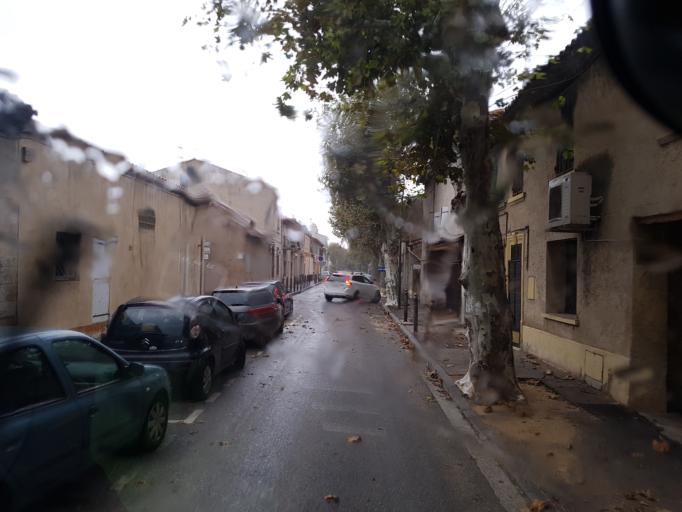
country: FR
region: Provence-Alpes-Cote d'Azur
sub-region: Departement des Bouches-du-Rhone
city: Gignac-la-Nerthe
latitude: 43.3934
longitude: 5.2359
